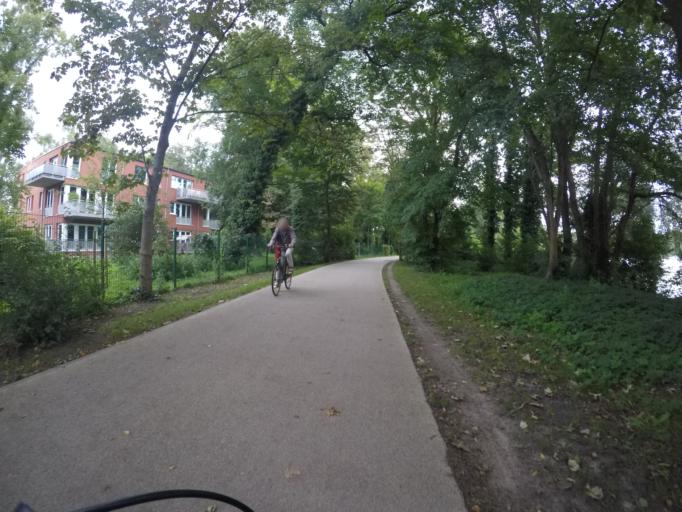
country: DE
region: Brandenburg
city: Potsdam
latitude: 52.3839
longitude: 13.0250
